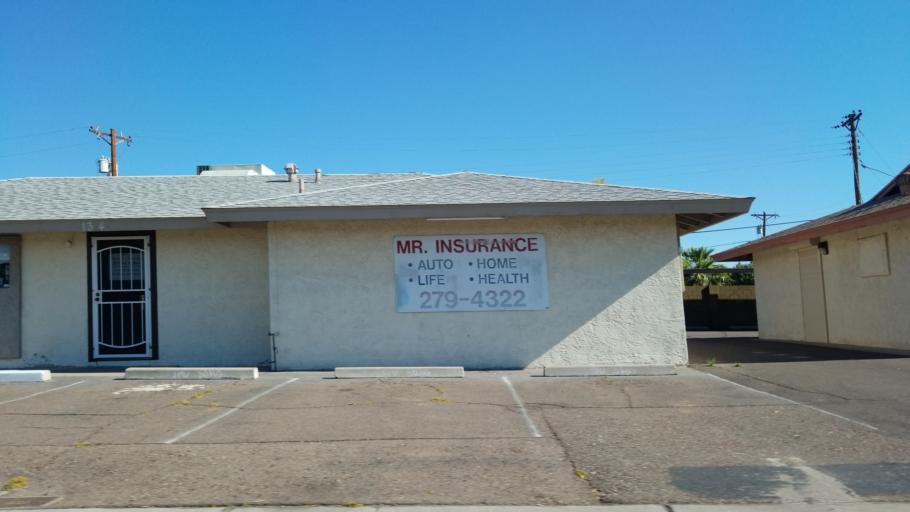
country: US
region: Arizona
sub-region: Maricopa County
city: Phoenix
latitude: 33.5097
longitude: -112.0897
